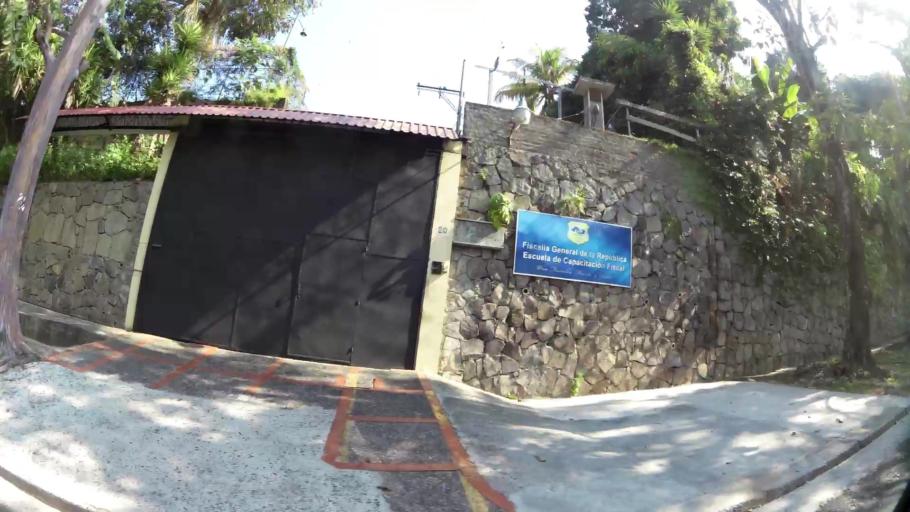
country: SV
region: La Libertad
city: Antiguo Cuscatlan
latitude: 13.6763
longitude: -89.2311
